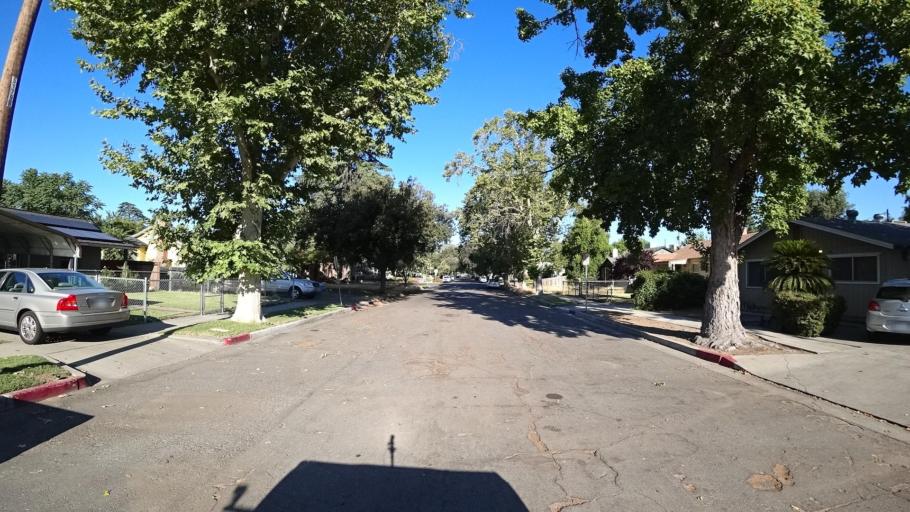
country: US
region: California
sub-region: Fresno County
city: Fresno
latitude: 36.7714
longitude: -119.7966
